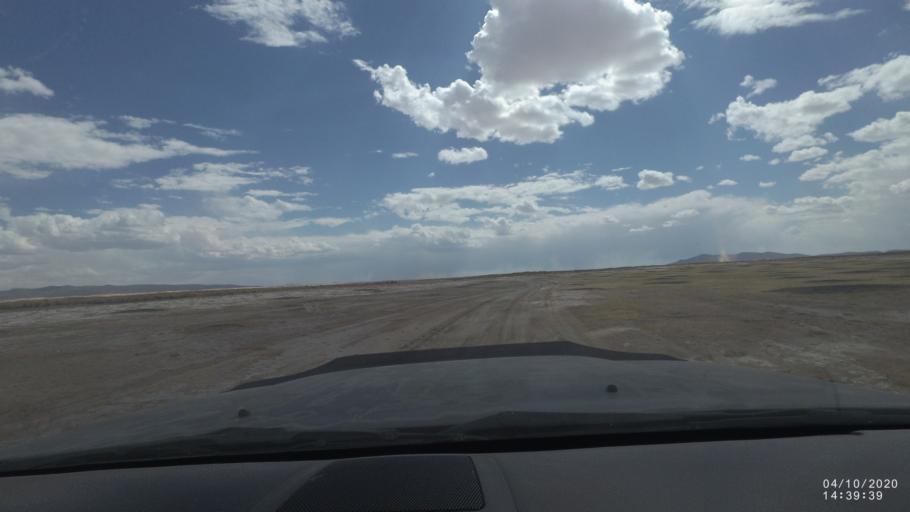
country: BO
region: Oruro
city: Poopo
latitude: -18.6781
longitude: -67.4871
